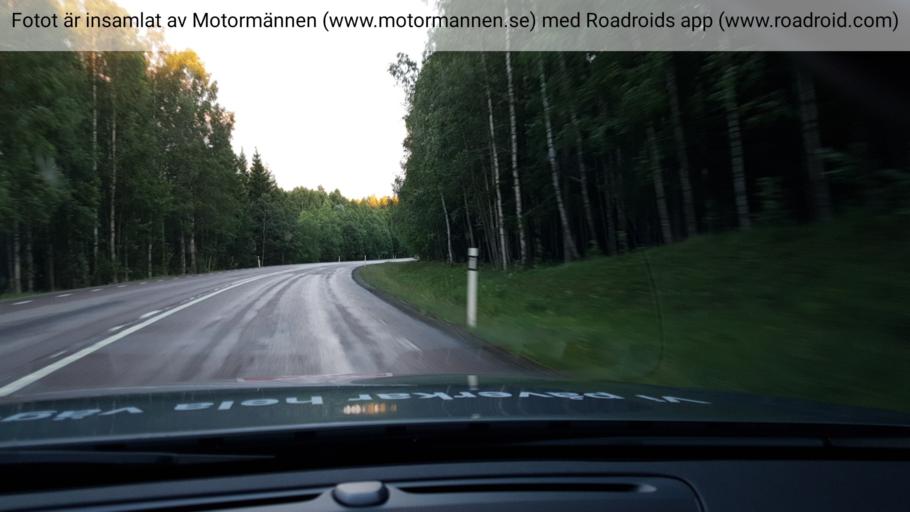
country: SE
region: Vaestmanland
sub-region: Skinnskattebergs Kommun
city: Skinnskatteberg
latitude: 59.9070
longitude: 15.7207
